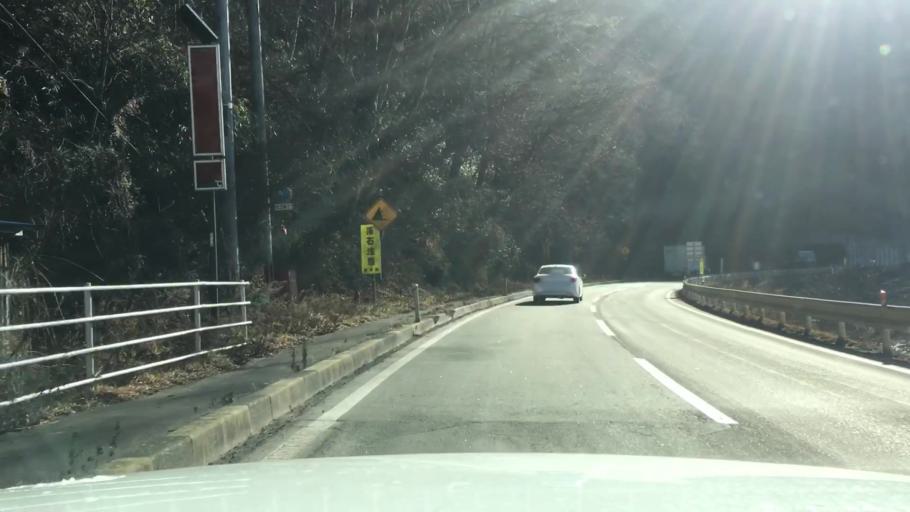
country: JP
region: Iwate
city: Miyako
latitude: 39.6078
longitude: 141.6521
